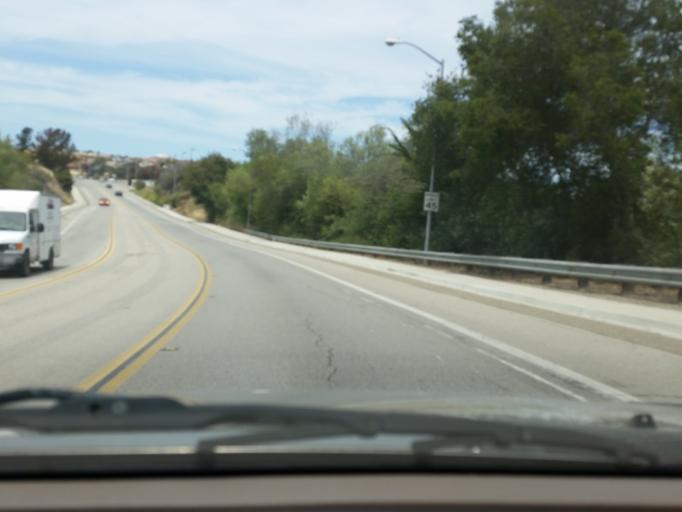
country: US
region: California
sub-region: San Luis Obispo County
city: Grover Beach
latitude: 35.1324
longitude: -120.6222
